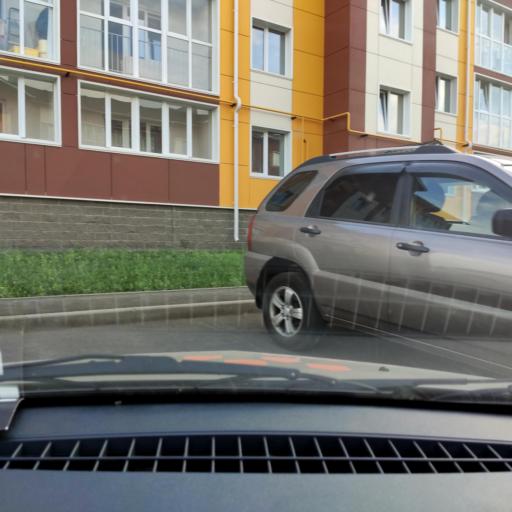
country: RU
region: Bashkortostan
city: Ufa
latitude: 54.5881
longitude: 55.9156
